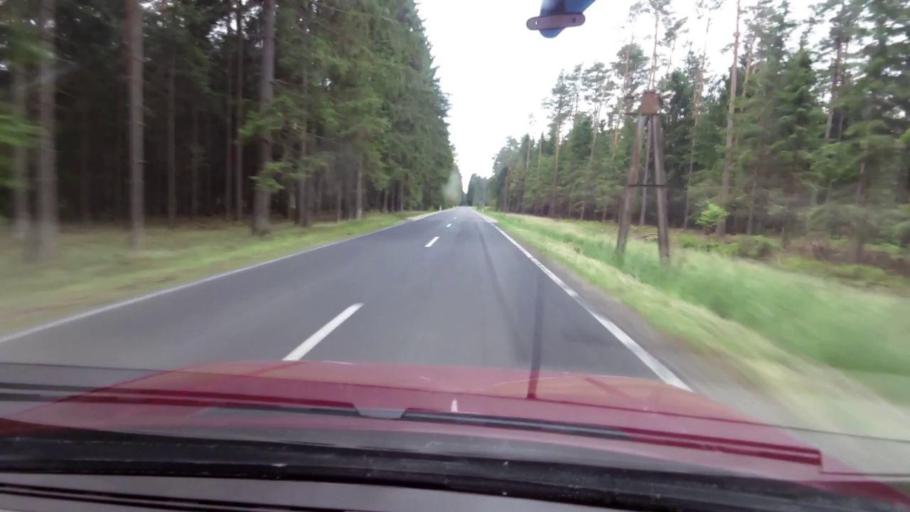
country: PL
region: West Pomeranian Voivodeship
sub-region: Powiat koszalinski
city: Polanow
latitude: 54.1419
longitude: 16.4885
